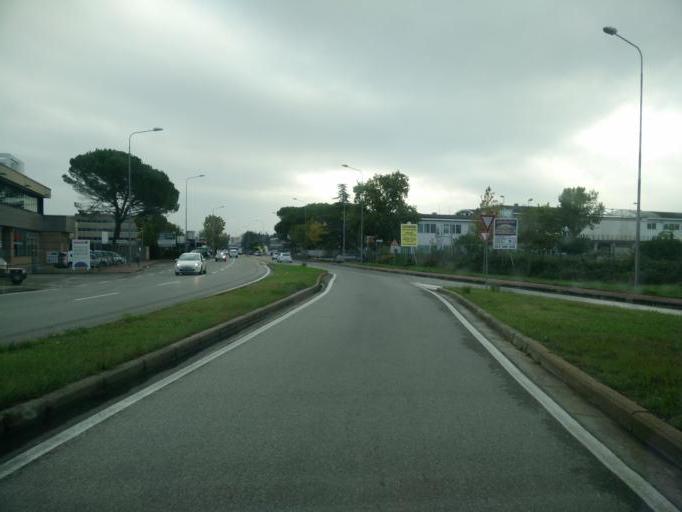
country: IT
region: Tuscany
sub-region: Province of Florence
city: Mantignano-Ugnano
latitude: 43.8067
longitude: 11.1783
